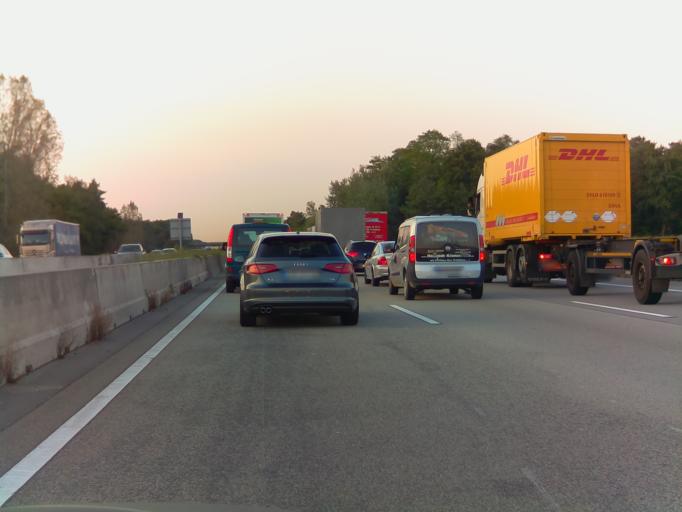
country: DE
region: Hesse
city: Viernheim
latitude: 49.5919
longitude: 8.5607
